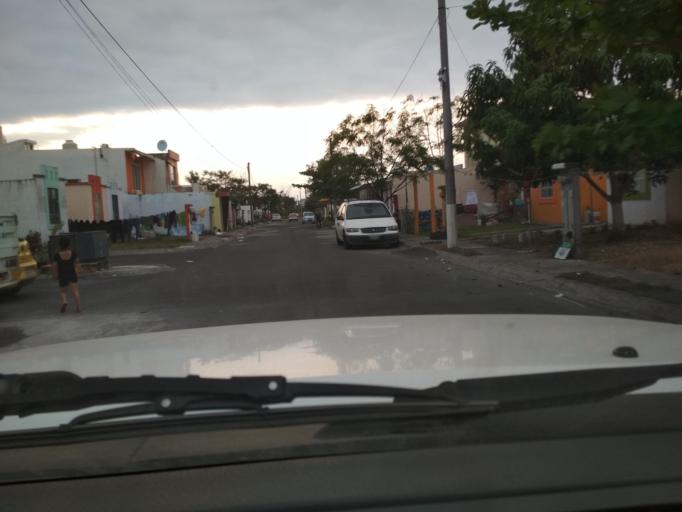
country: MX
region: Veracruz
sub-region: Medellin
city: Fraccionamiento Arboledas San Ramon
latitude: 19.0919
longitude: -96.1595
